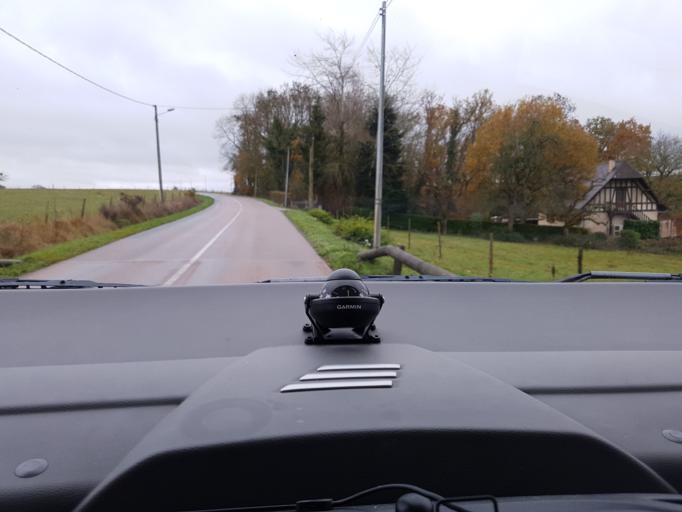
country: FR
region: Haute-Normandie
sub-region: Departement de l'Eure
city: Pont-Saint-Pierre
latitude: 49.3120
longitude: 1.3106
